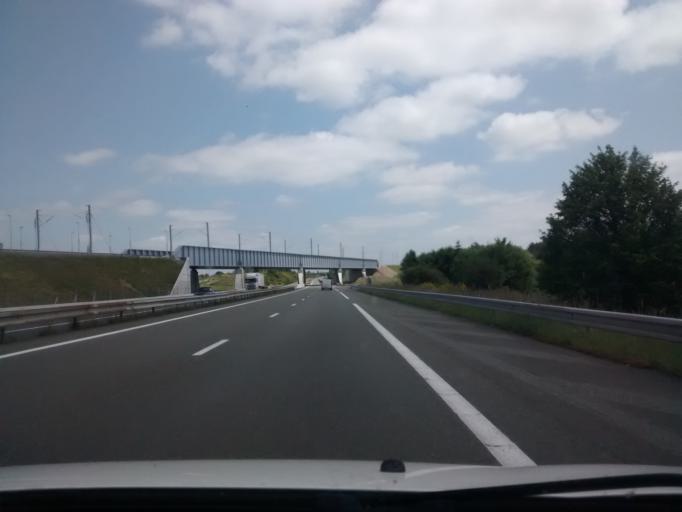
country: FR
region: Pays de la Loire
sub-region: Departement de la Mayenne
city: Louverne
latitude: 48.0994
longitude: -0.7156
